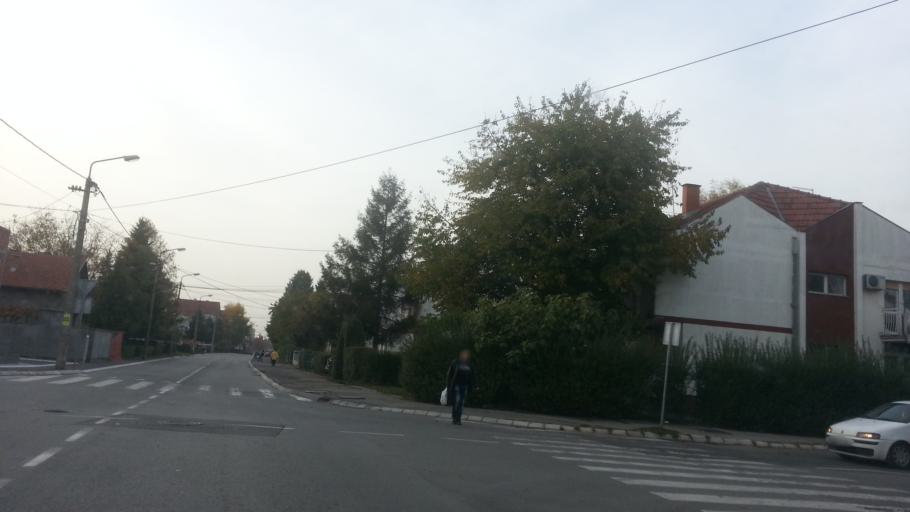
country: RS
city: Novi Banovci
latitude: 44.8975
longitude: 20.2841
